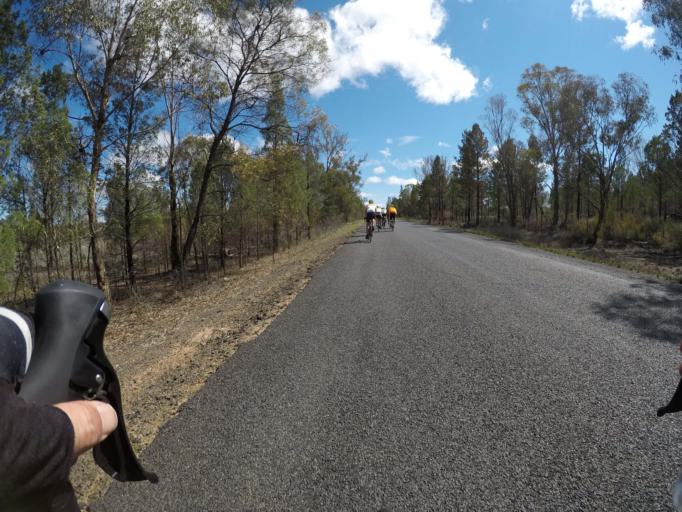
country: AU
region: New South Wales
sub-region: Parkes
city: Peak Hill
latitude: -32.6301
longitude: 148.5492
